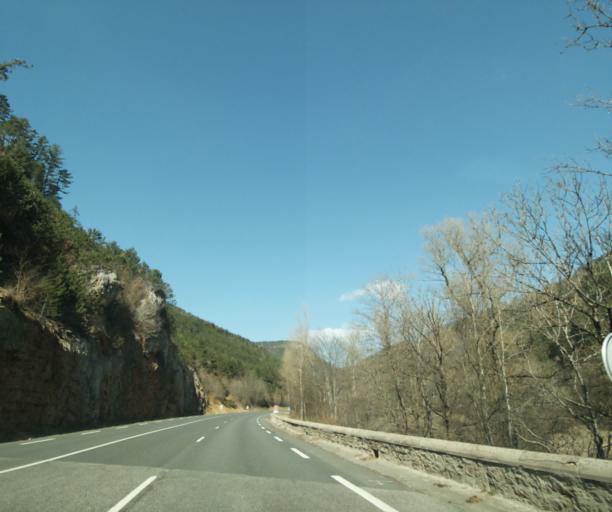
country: FR
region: Languedoc-Roussillon
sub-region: Departement de la Lozere
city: Mende
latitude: 44.4970
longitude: 3.4629
